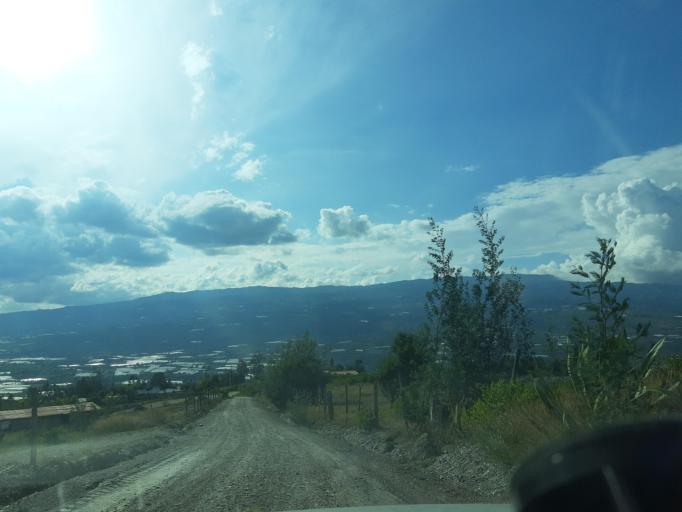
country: CO
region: Boyaca
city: Villa de Leiva
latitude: 5.6673
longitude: -73.5564
